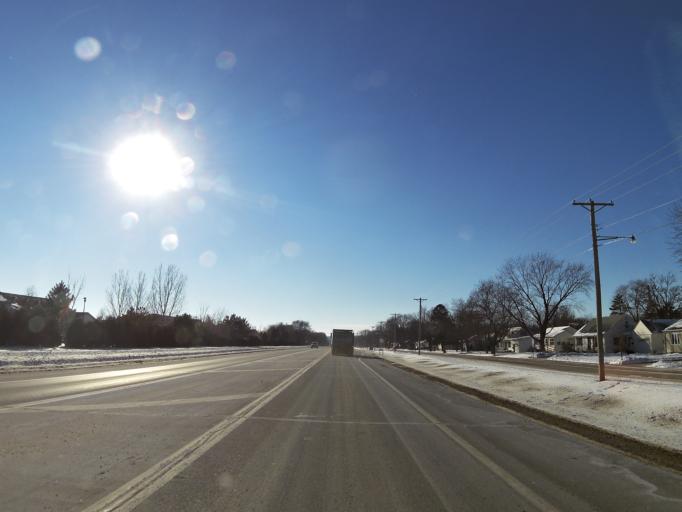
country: US
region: Minnesota
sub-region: Carver County
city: Chaska
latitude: 44.7996
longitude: -93.5833
